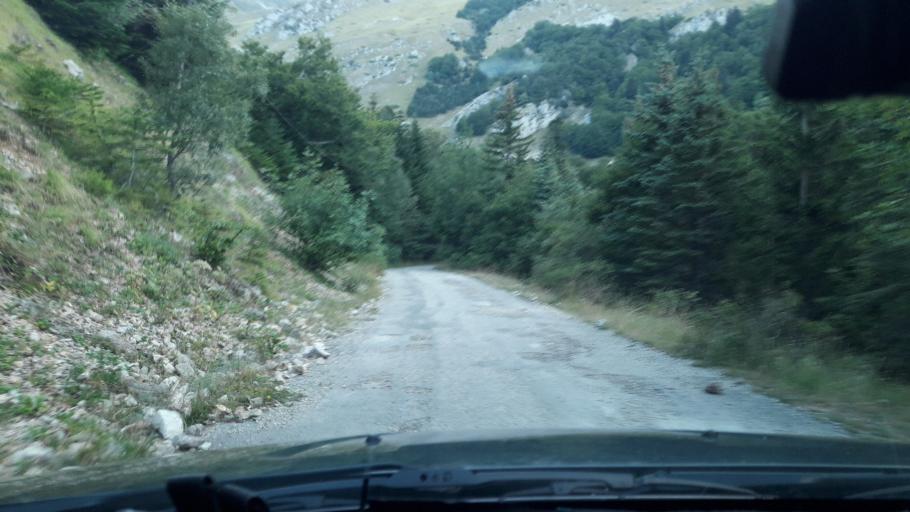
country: FR
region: Rhone-Alpes
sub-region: Departement de l'Isere
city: Mens
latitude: 44.7297
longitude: 5.6667
